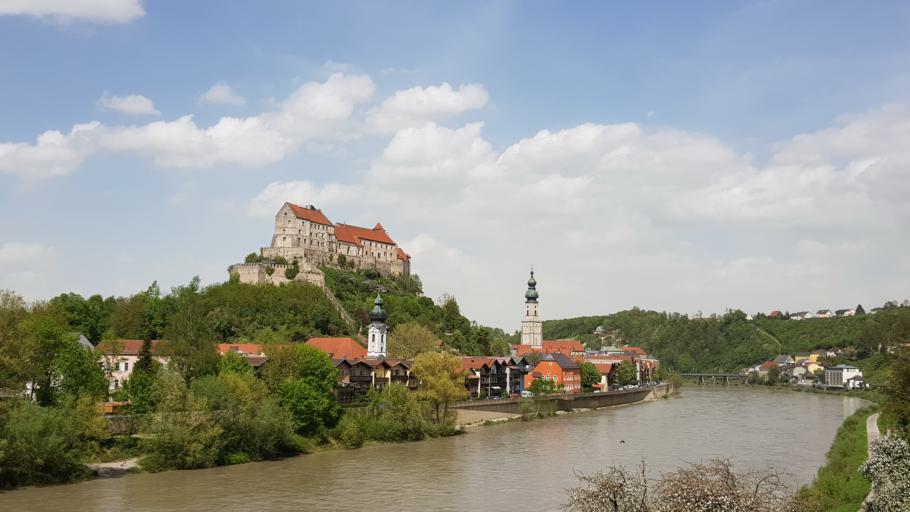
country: DE
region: Bavaria
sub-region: Upper Bavaria
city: Burghausen
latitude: 48.1518
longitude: 12.8271
